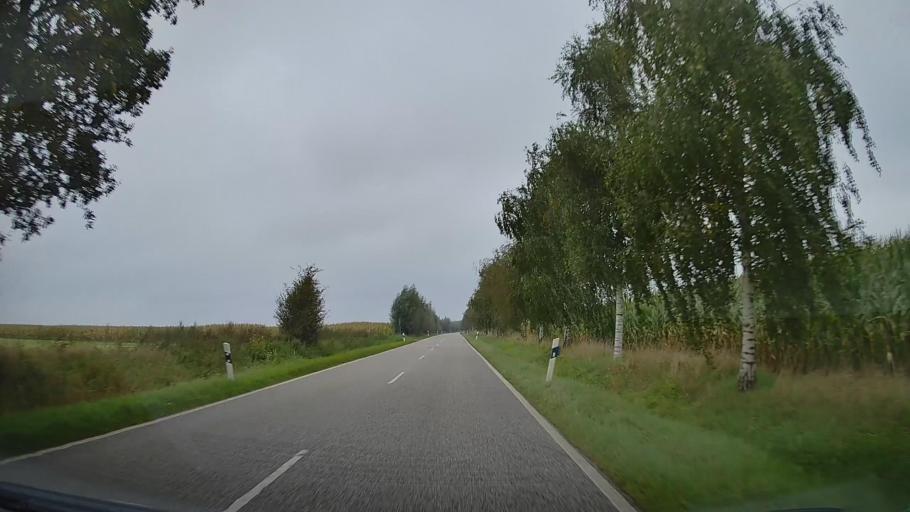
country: DE
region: Mecklenburg-Vorpommern
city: Blowatz
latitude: 53.9560
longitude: 11.5671
